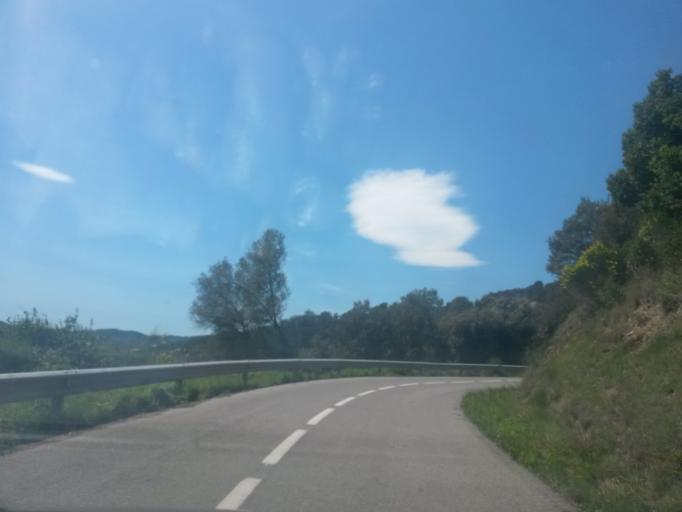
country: ES
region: Catalonia
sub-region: Provincia de Girona
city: Madremanya
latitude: 41.9331
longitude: 2.9258
